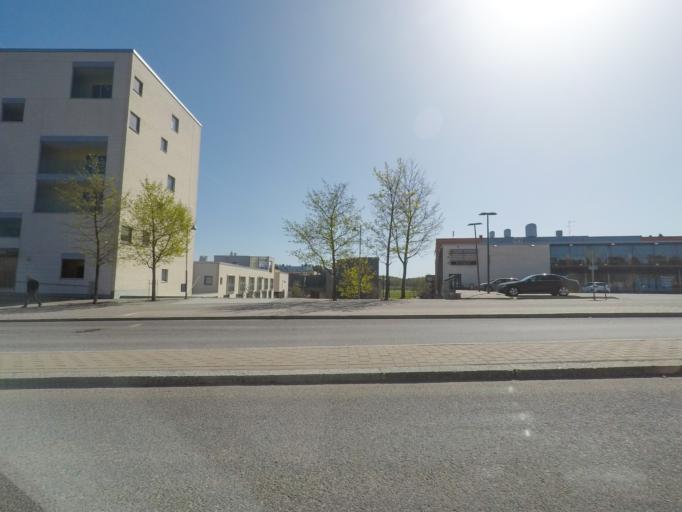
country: FI
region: Uusimaa
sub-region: Helsinki
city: Vantaa
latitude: 60.2344
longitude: 25.0325
